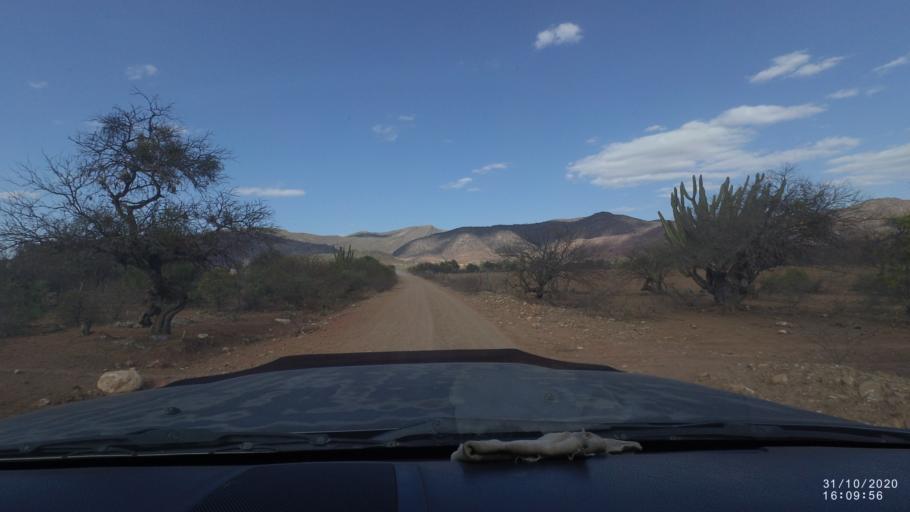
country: BO
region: Chuquisaca
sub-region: Provincia Zudanez
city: Mojocoya
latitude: -18.3846
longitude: -64.6340
